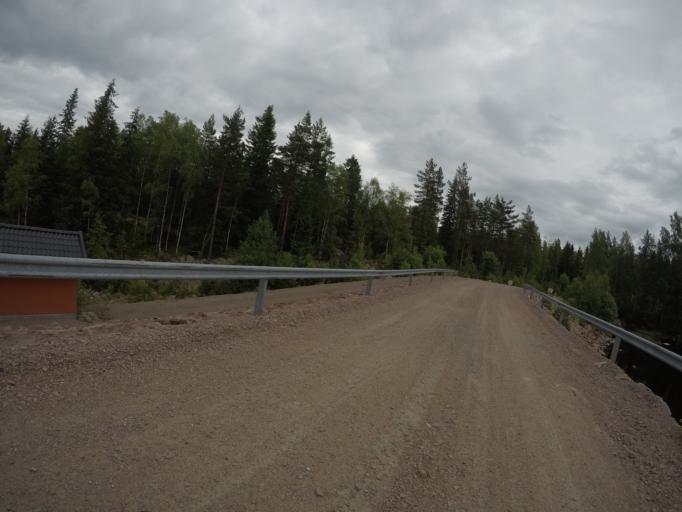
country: SE
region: Dalarna
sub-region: Ludvika Kommun
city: Abborrberget
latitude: 60.0731
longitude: 14.5636
